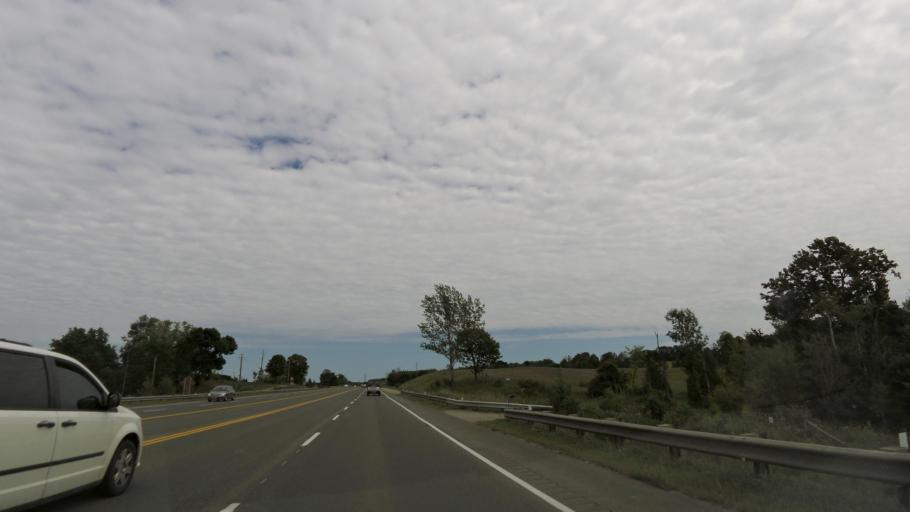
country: CA
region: Ontario
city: Bradford West Gwillimbury
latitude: 44.0343
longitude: -79.5710
